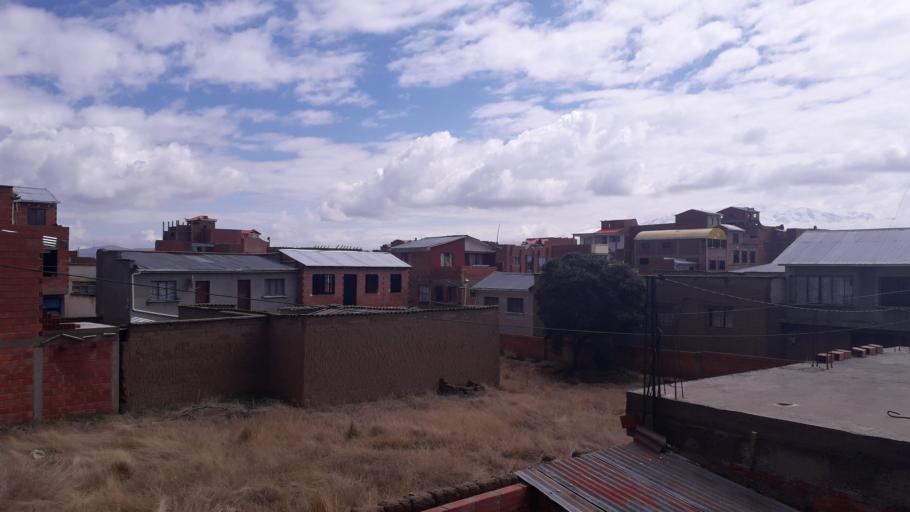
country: BO
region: La Paz
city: Achacachi
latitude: -16.0467
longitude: -68.6865
